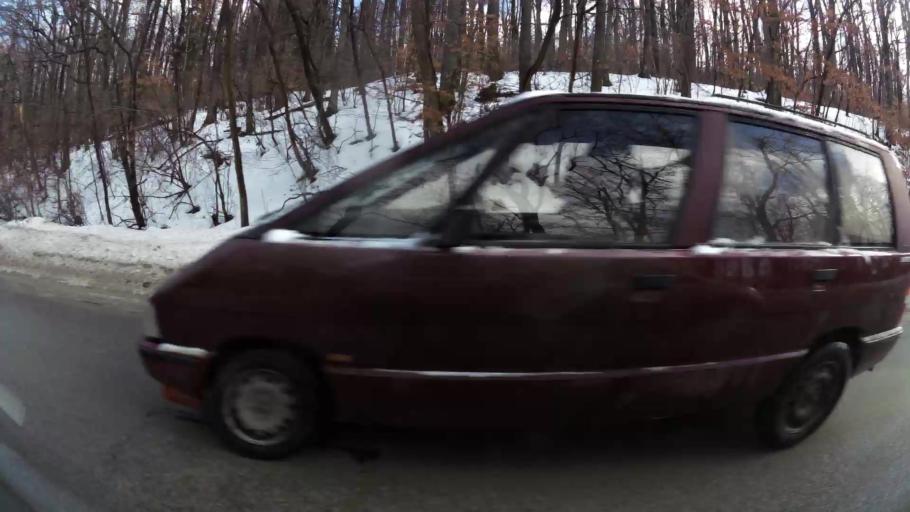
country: BG
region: Sofiya
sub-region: Obshtina Bozhurishte
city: Bozhurishte
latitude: 42.6366
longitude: 23.2218
